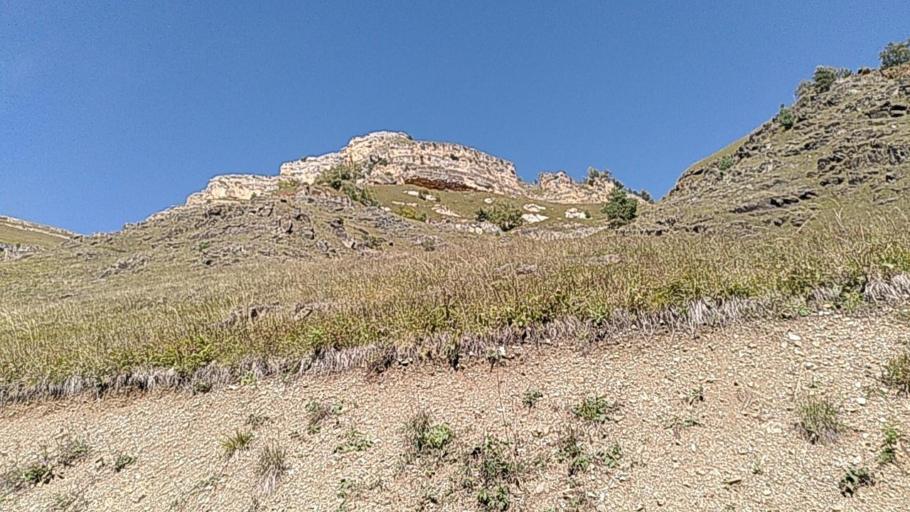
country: RU
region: Kabardino-Balkariya
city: Kamennomostskoye
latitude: 43.6801
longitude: 42.8200
